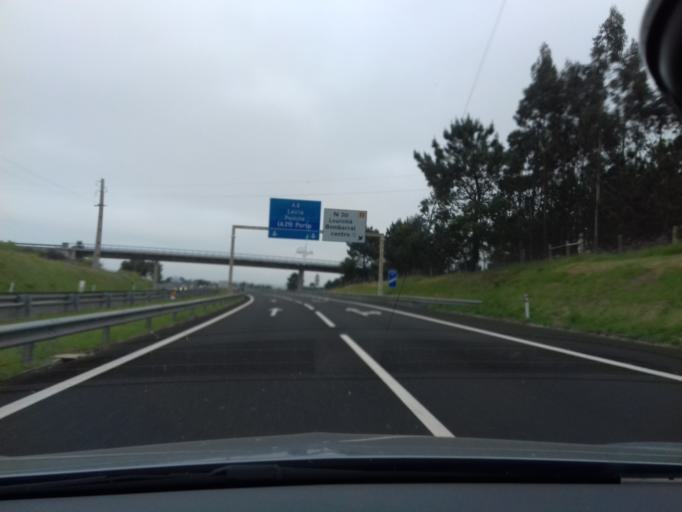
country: PT
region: Leiria
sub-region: Bombarral
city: Bombarral
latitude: 39.2536
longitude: -9.1648
